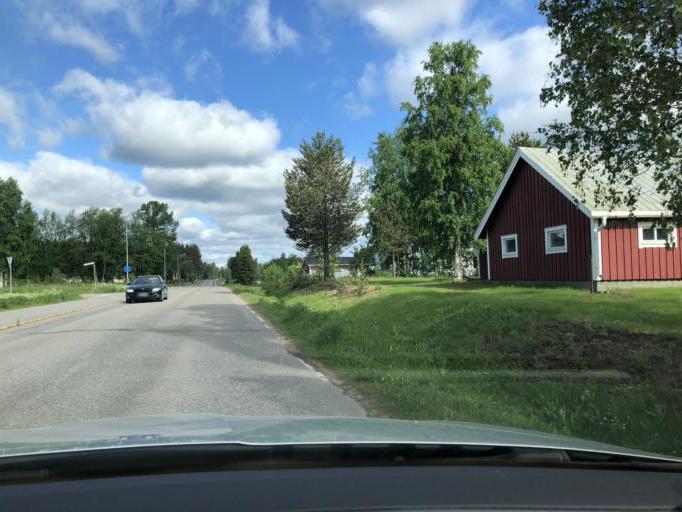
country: SE
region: Norrbotten
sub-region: Pajala Kommun
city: Pajala
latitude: 67.2204
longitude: 23.3499
